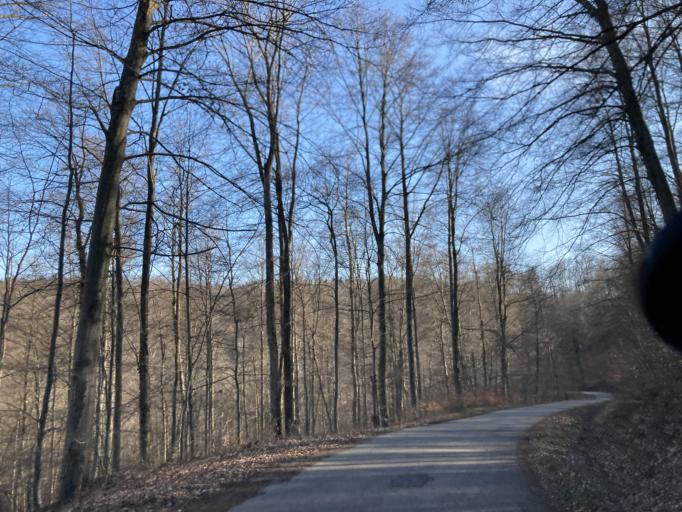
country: DE
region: Baden-Wuerttemberg
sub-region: Tuebingen Region
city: Ofterdingen
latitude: 48.3741
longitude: 9.0237
